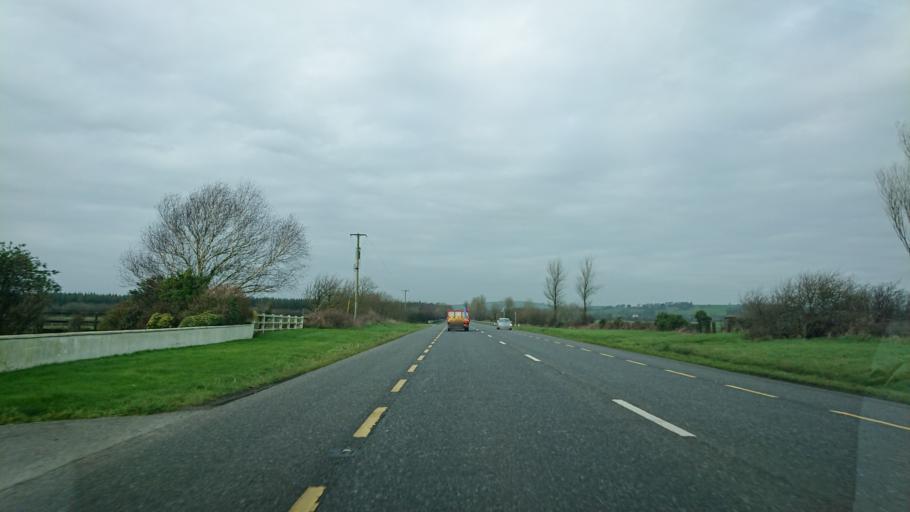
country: IE
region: Munster
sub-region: County Cork
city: Castlemartyr
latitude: 51.9379
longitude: -7.9661
